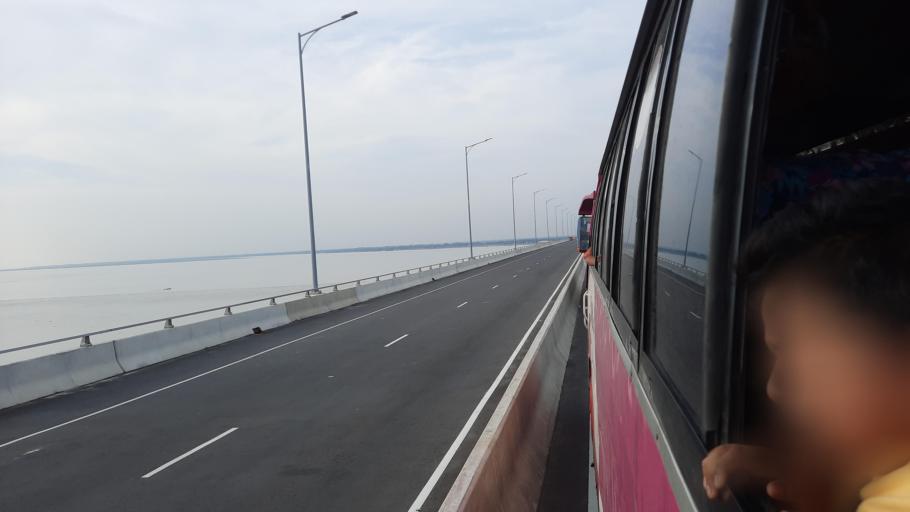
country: BD
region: Dhaka
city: Char Bhadrasan
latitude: 23.4431
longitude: 90.2611
